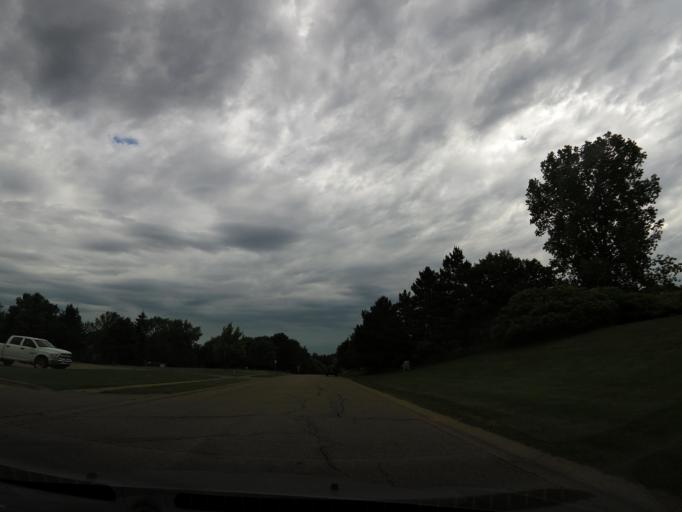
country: US
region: Minnesota
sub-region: Scott County
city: Prior Lake
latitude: 44.7074
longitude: -93.4355
